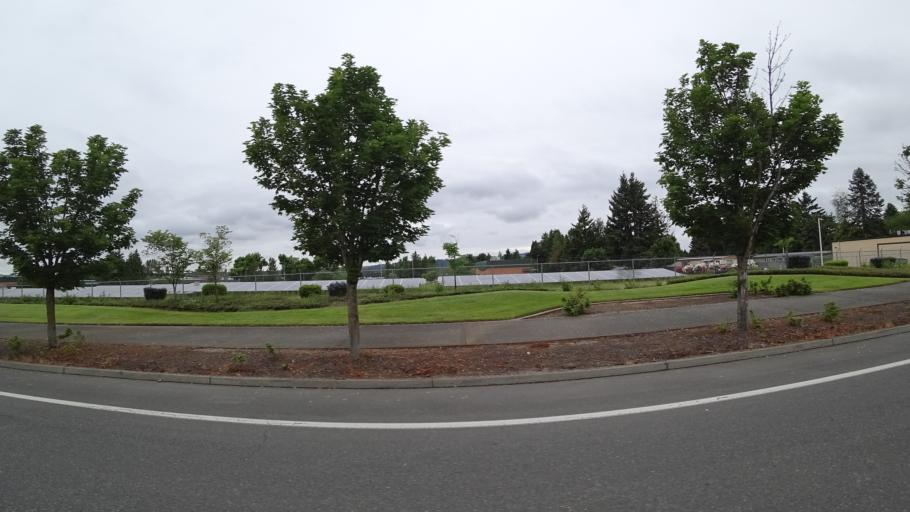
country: US
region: Oregon
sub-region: Multnomah County
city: Fairview
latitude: 45.5451
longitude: -122.4573
